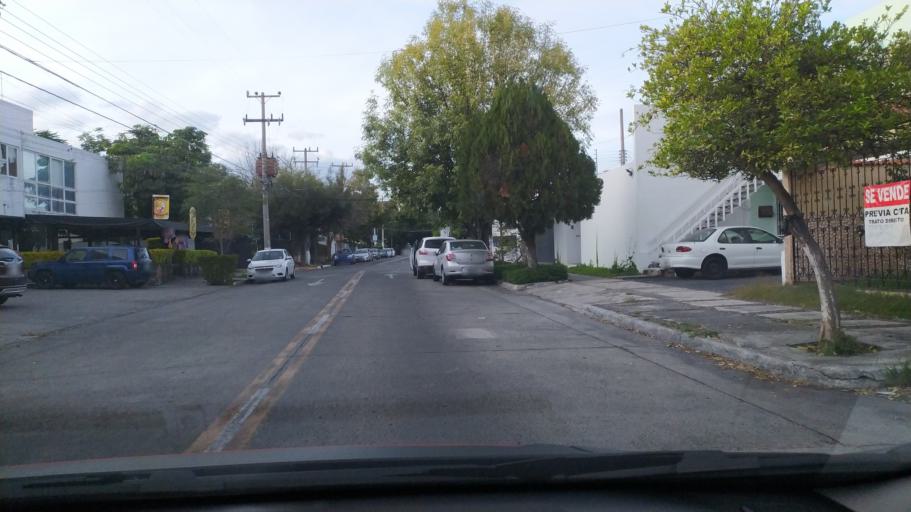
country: MX
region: Jalisco
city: Guadalajara
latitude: 20.6611
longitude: -103.4043
